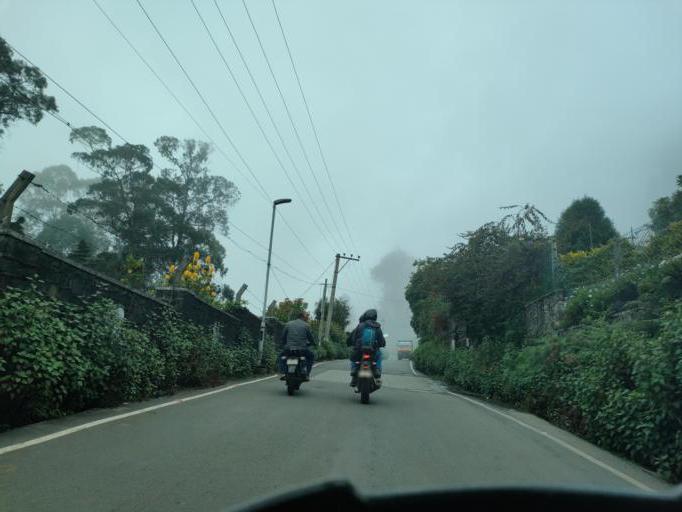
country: IN
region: Tamil Nadu
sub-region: Dindigul
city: Kodaikanal
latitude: 10.2367
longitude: 77.4835
